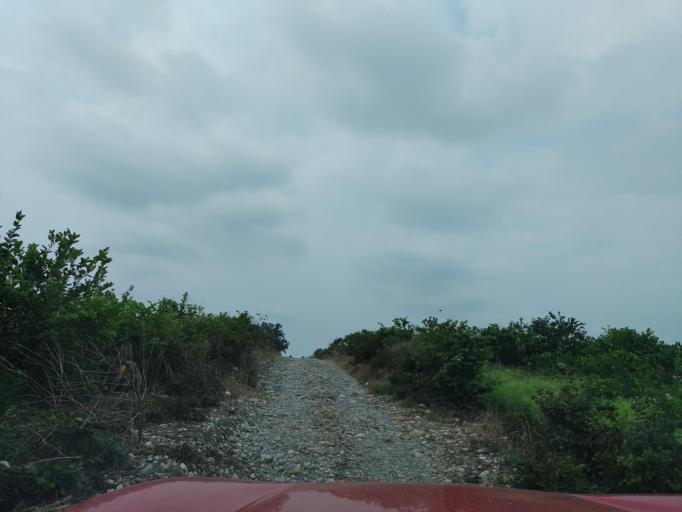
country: MX
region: Veracruz
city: Agua Dulce
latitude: 20.3415
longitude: -97.2953
